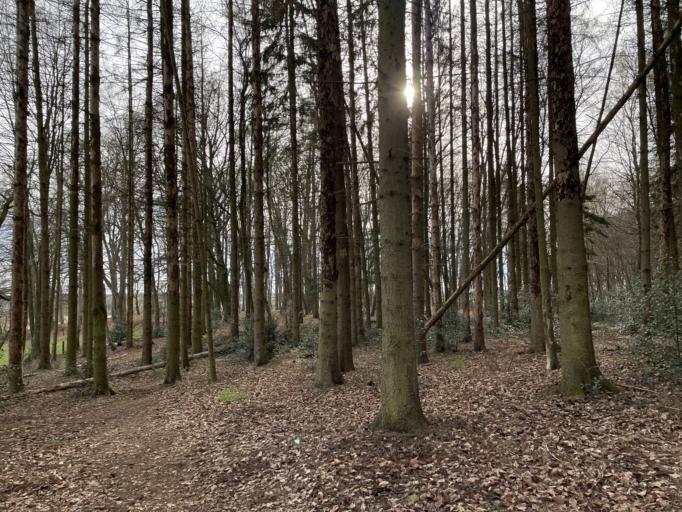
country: DE
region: North Rhine-Westphalia
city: Porta Westfalica
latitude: 52.2324
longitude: 8.9612
